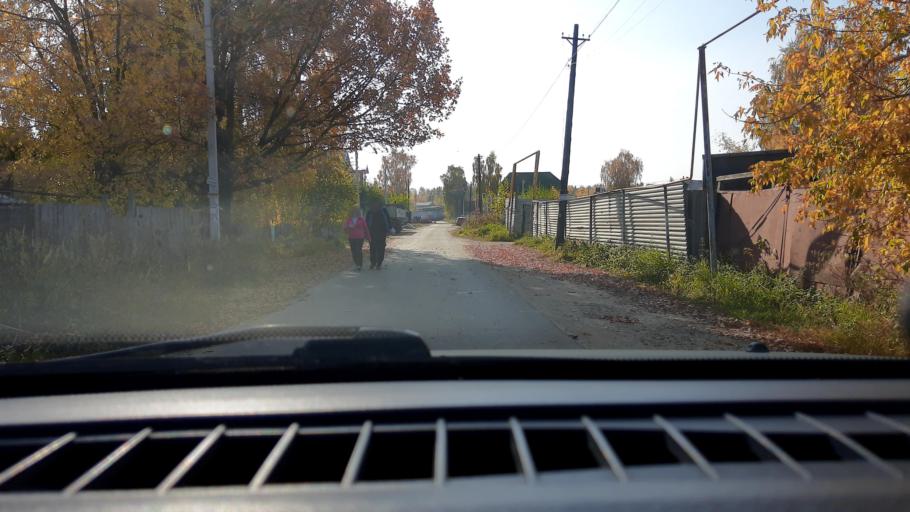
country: RU
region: Nizjnij Novgorod
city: Gorbatovka
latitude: 56.3306
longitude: 43.8298
